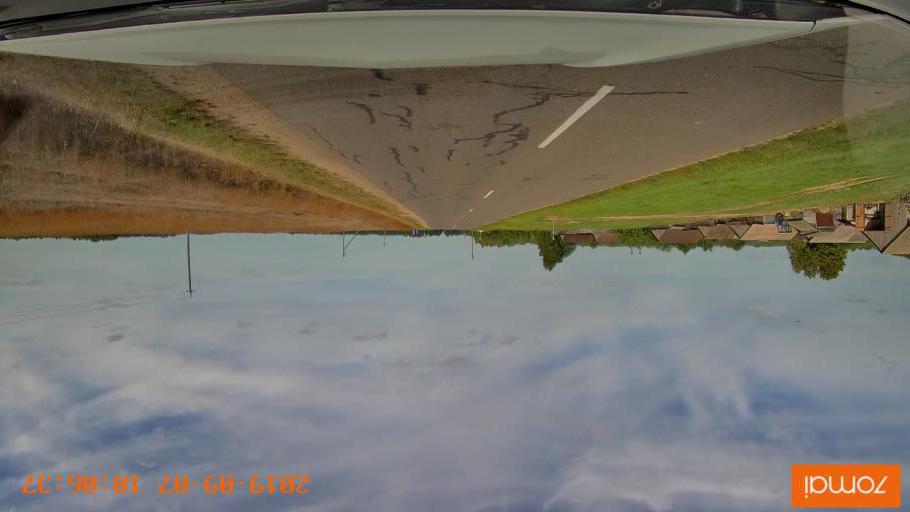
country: BY
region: Grodnenskaya
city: Voranava
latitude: 54.0644
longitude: 25.4027
